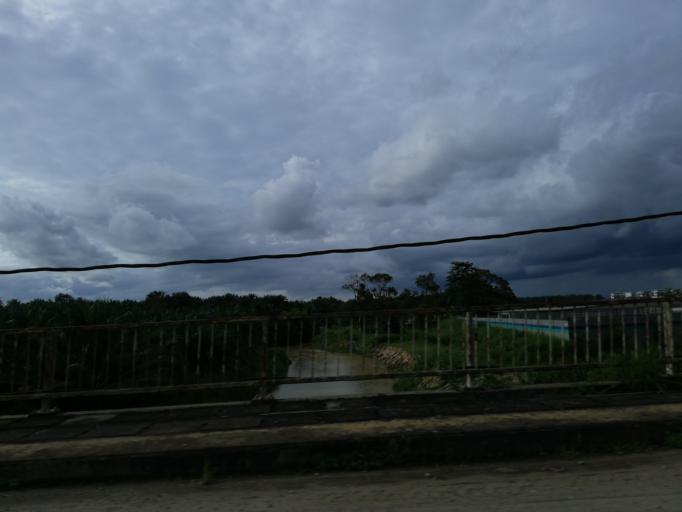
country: MY
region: Penang
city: Tasek Glugor
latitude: 5.5036
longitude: 100.6181
